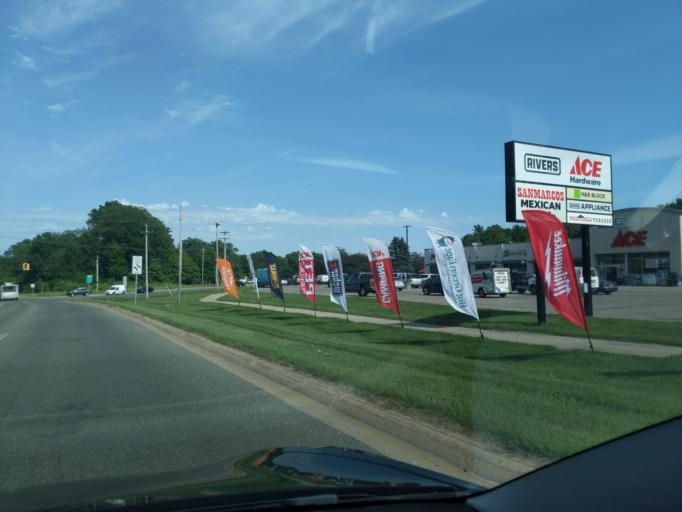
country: US
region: Michigan
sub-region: Muskegon County
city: Whitehall
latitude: 43.4089
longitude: -86.3189
